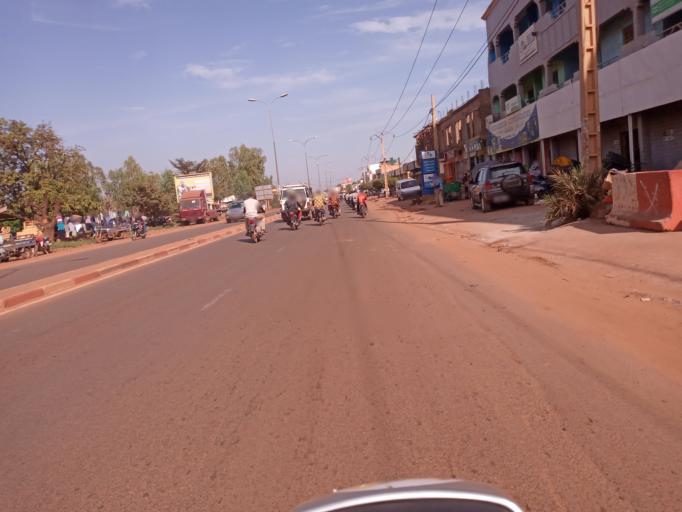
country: ML
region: Bamako
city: Bamako
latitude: 12.6654
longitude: -7.9352
